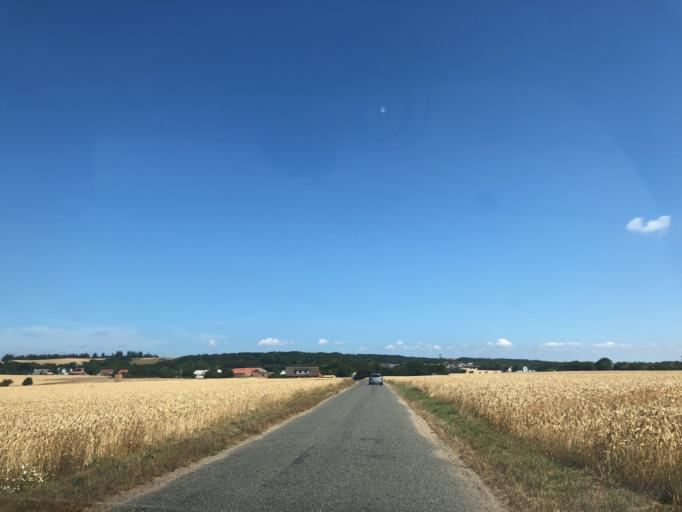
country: DK
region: North Denmark
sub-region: Morso Kommune
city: Nykobing Mors
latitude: 56.8161
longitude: 8.9973
